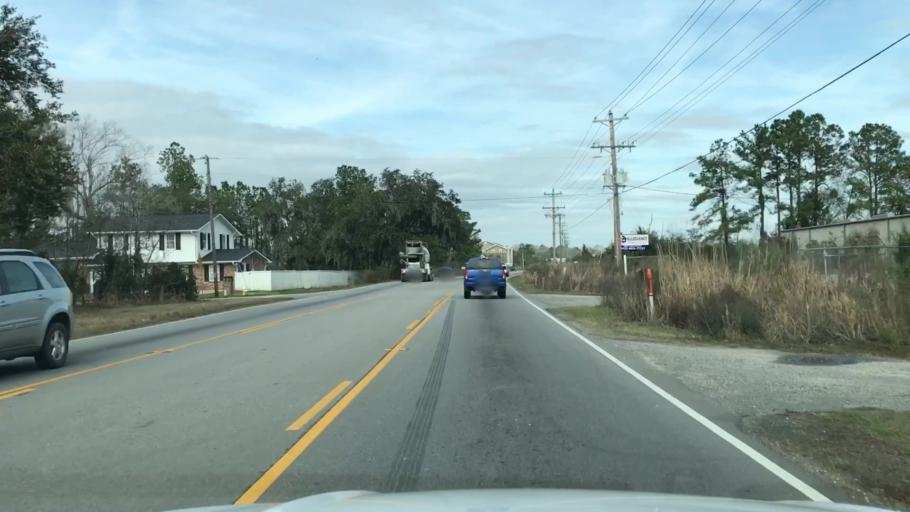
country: US
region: South Carolina
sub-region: Charleston County
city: Shell Point
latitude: 32.7960
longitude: -80.1083
